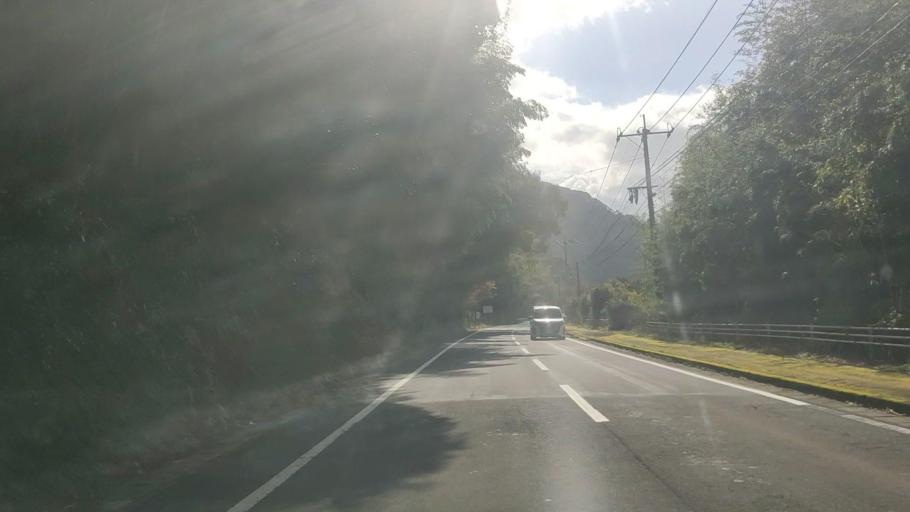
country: JP
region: Kagoshima
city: Okuchi-shinohara
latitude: 31.9829
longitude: 130.7428
